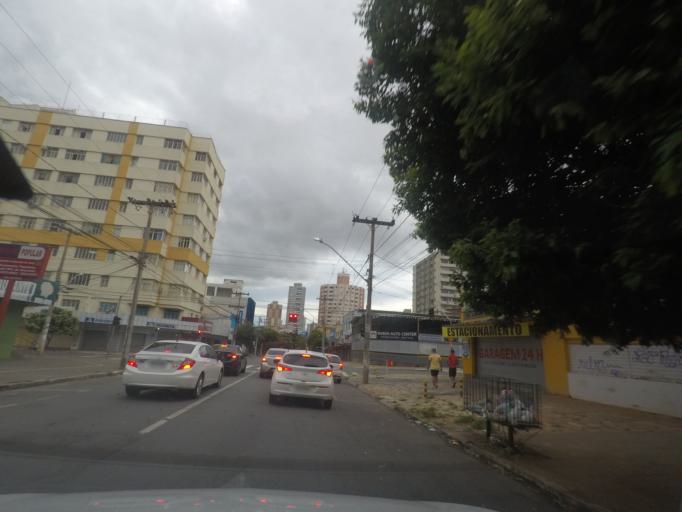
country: BR
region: Goias
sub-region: Goiania
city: Goiania
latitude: -16.6748
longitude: -49.2533
